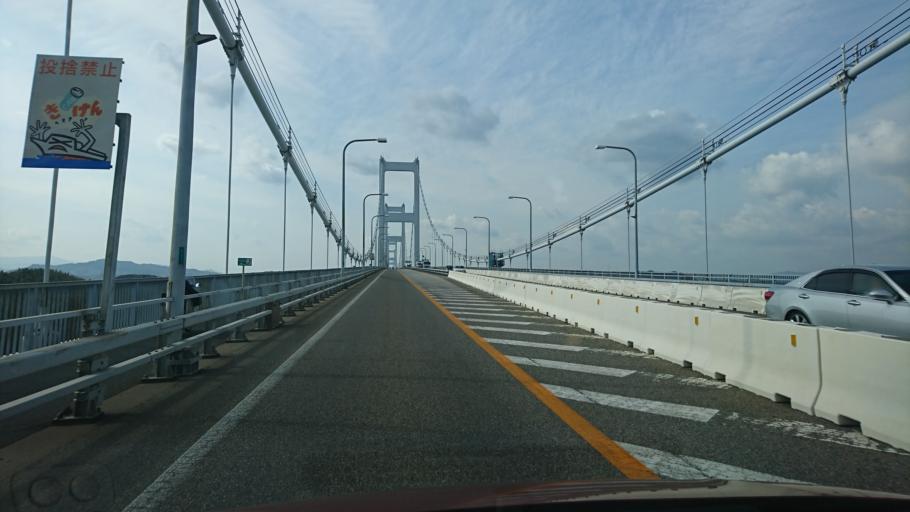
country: JP
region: Hiroshima
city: Innoshima
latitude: 34.1263
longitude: 133.0138
